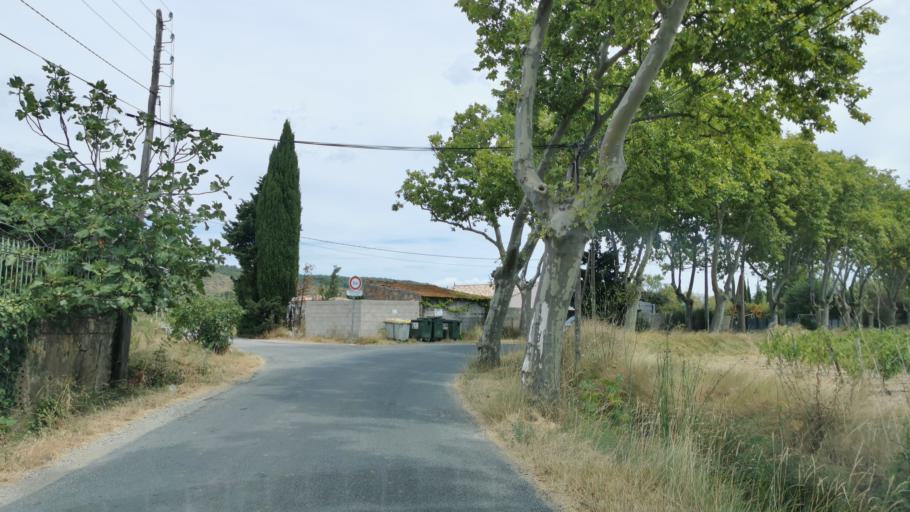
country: FR
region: Languedoc-Roussillon
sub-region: Departement de l'Aude
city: Bize-Minervois
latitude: 43.3046
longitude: 2.8307
